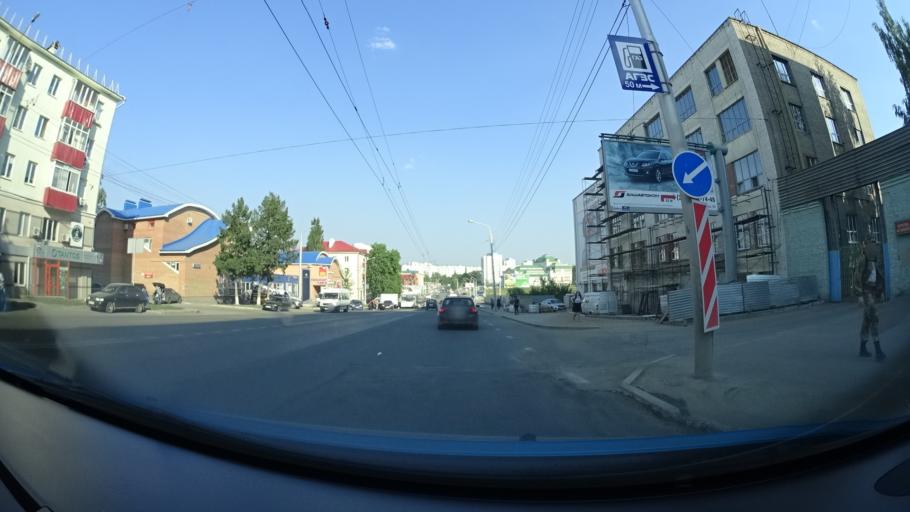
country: RU
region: Bashkortostan
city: Ufa
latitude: 54.7520
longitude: 56.0139
